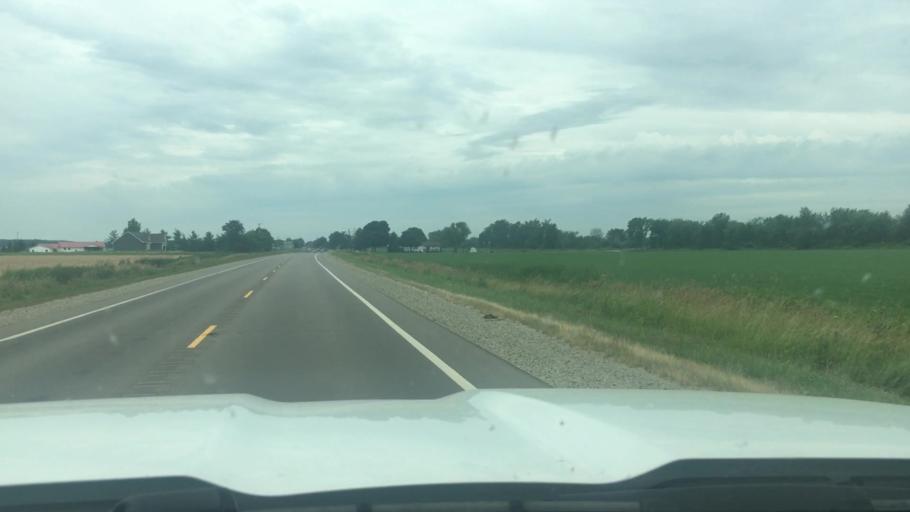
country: US
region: Michigan
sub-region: Clinton County
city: Fowler
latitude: 43.0017
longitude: -84.7146
